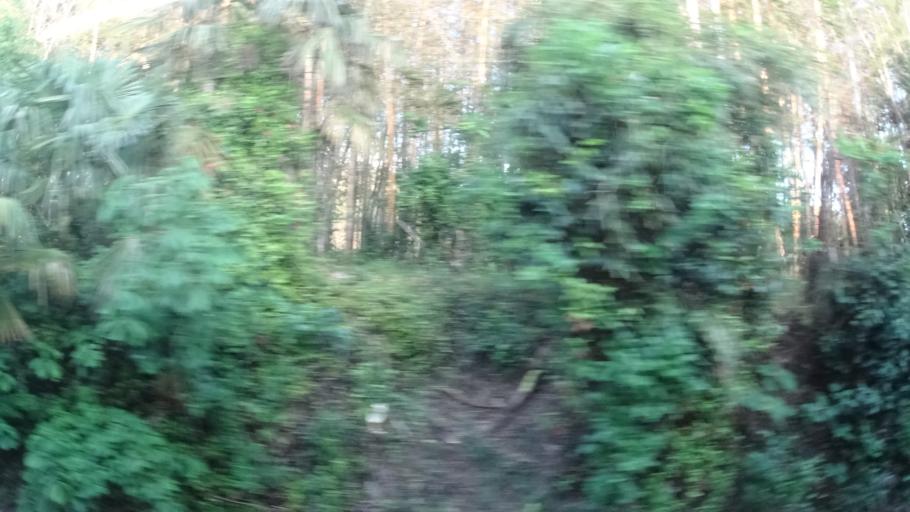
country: JP
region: Aichi
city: Toyohashi
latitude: 34.7079
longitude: 137.3689
